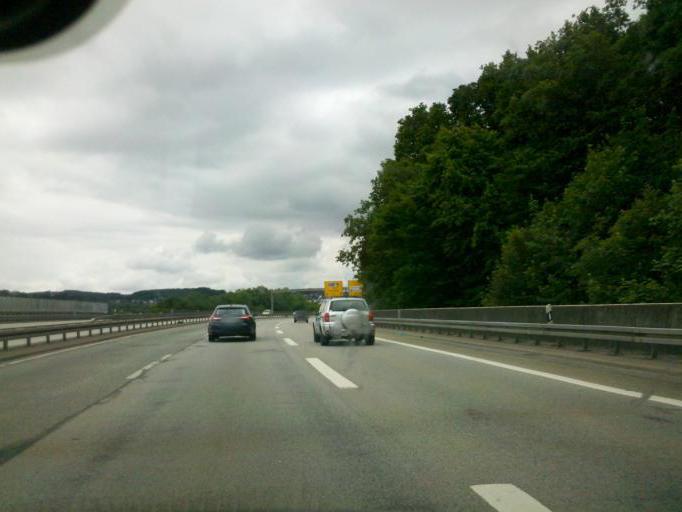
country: DE
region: North Rhine-Westphalia
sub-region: Regierungsbezirk Arnsberg
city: Siegen
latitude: 50.9006
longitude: 8.0205
